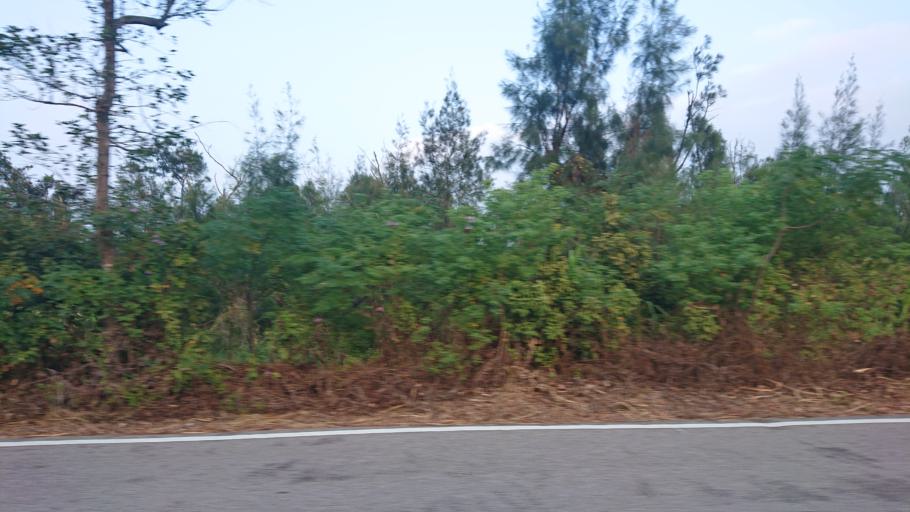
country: CN
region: Fujian
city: Shijing
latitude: 24.4950
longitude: 118.4450
